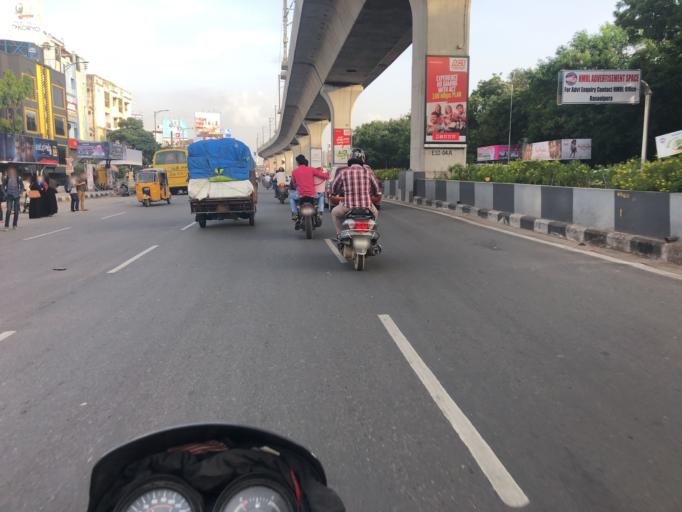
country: IN
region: Telangana
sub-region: Rangareddi
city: Kukatpalli
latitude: 17.4464
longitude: 78.4390
